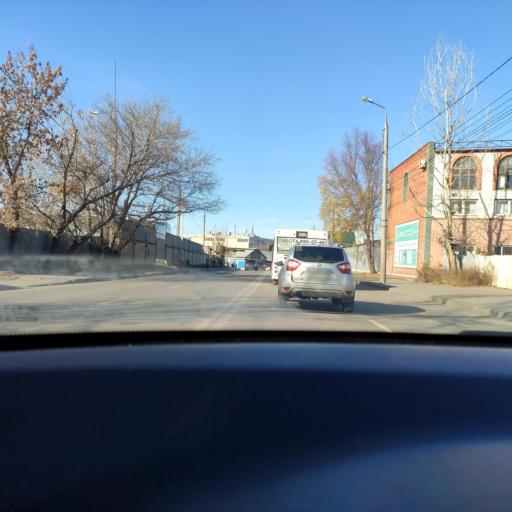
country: RU
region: Samara
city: Samara
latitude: 53.1849
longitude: 50.1484
